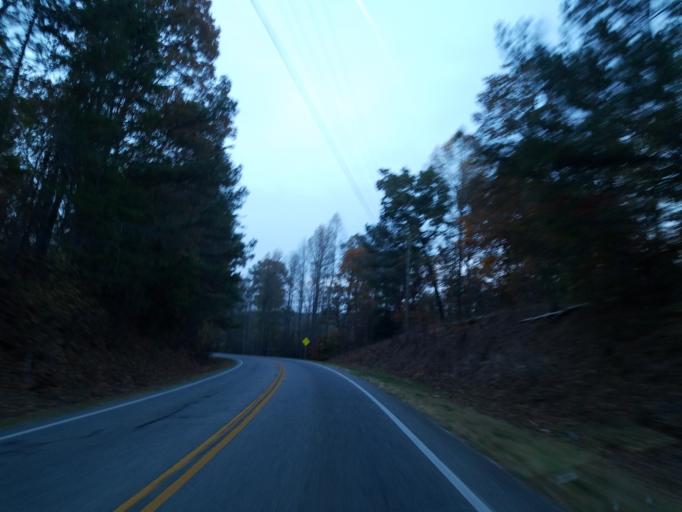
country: US
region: Georgia
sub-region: Gilmer County
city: Ellijay
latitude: 34.5514
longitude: -84.5994
